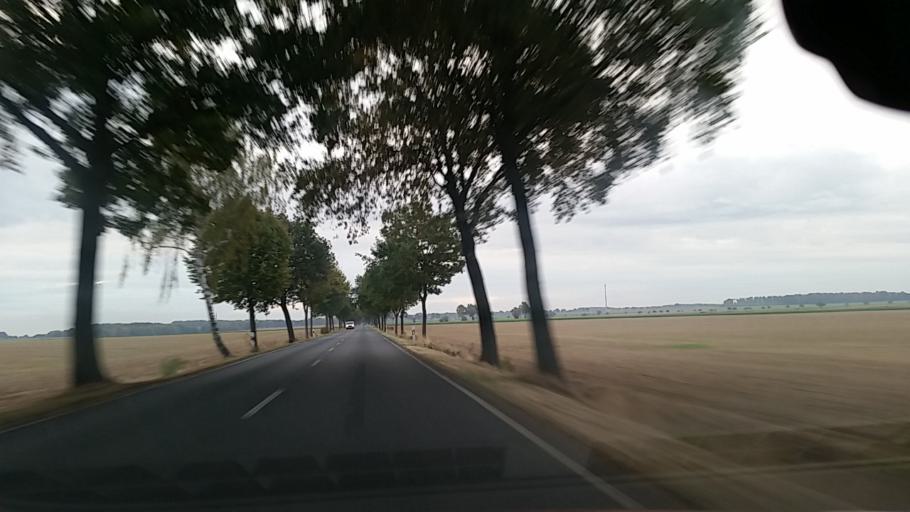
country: DE
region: Lower Saxony
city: Hankensbuttel
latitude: 52.7411
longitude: 10.5687
